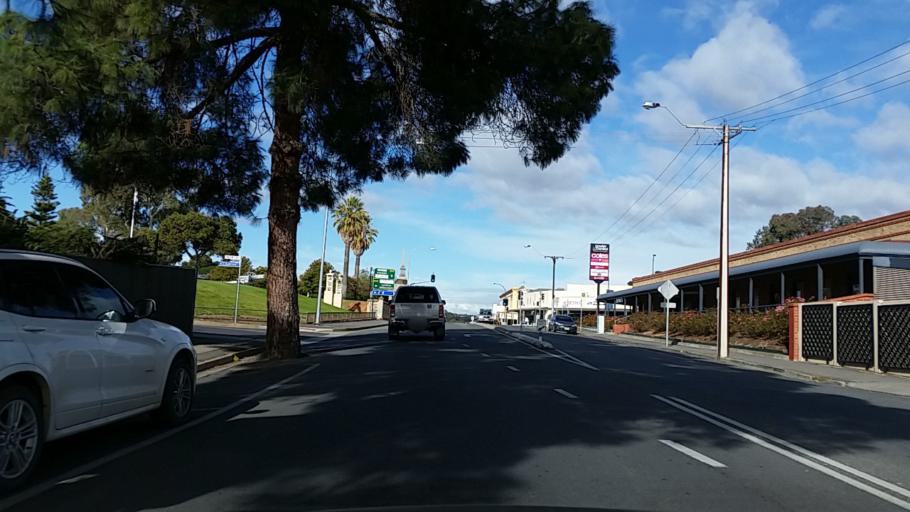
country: AU
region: South Australia
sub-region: Gawler
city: Gawler
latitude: -34.5952
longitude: 138.7490
